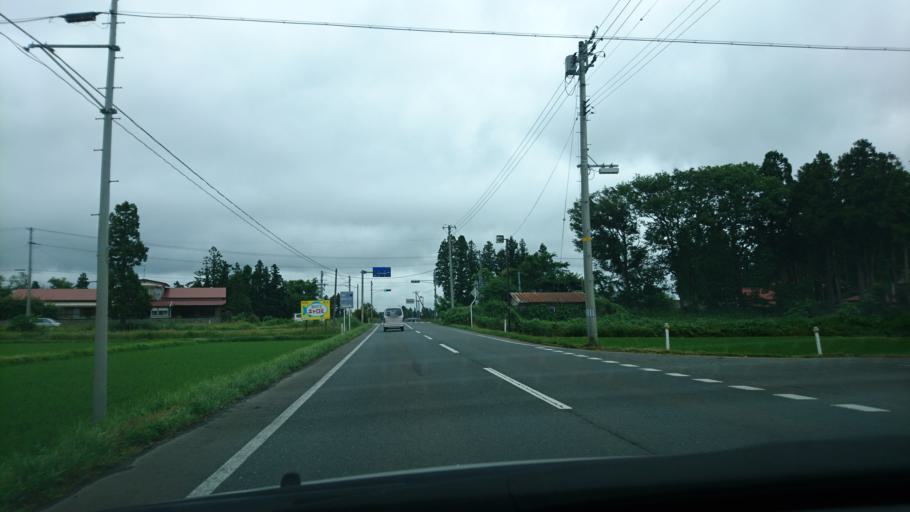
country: JP
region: Iwate
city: Mizusawa
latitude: 39.1184
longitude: 141.0528
